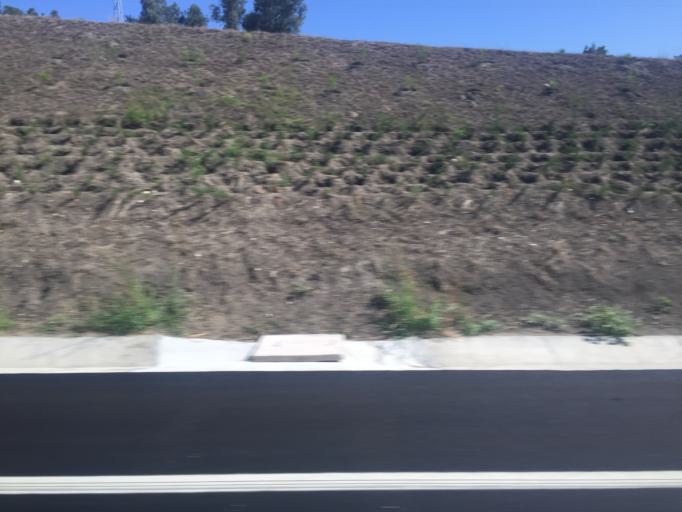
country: TR
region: Bursa
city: Gorukle
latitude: 40.2457
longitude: 28.7577
